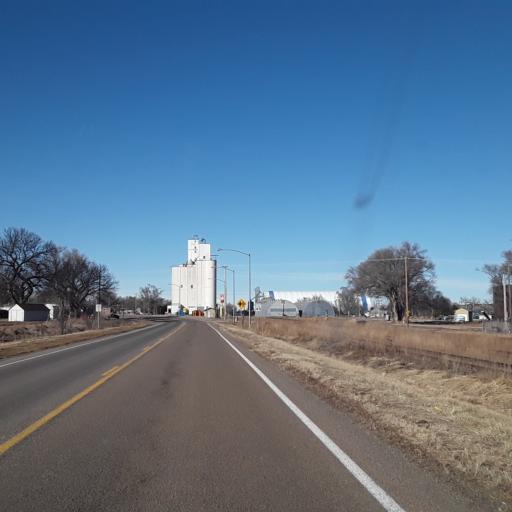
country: US
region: Nebraska
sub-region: Frontier County
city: Stockville
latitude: 40.6554
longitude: -100.6174
